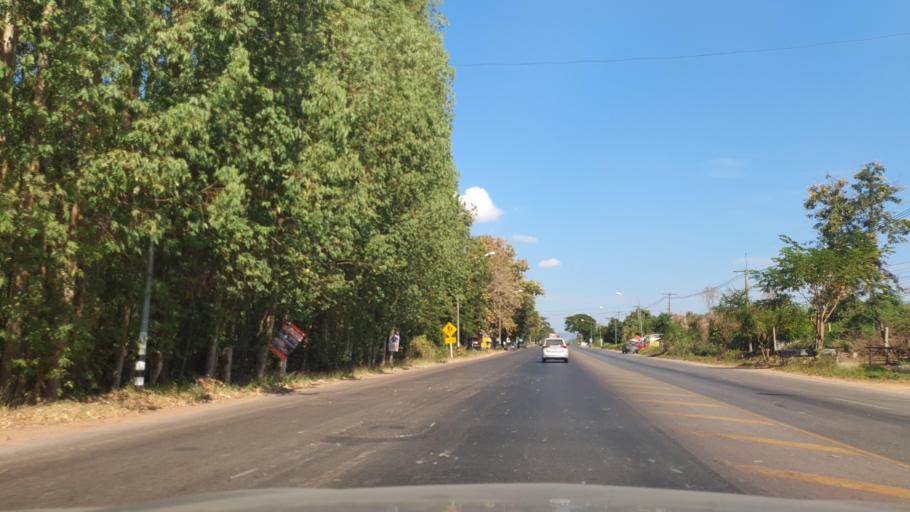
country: TH
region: Kalasin
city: Somdet
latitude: 16.7251
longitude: 103.7606
